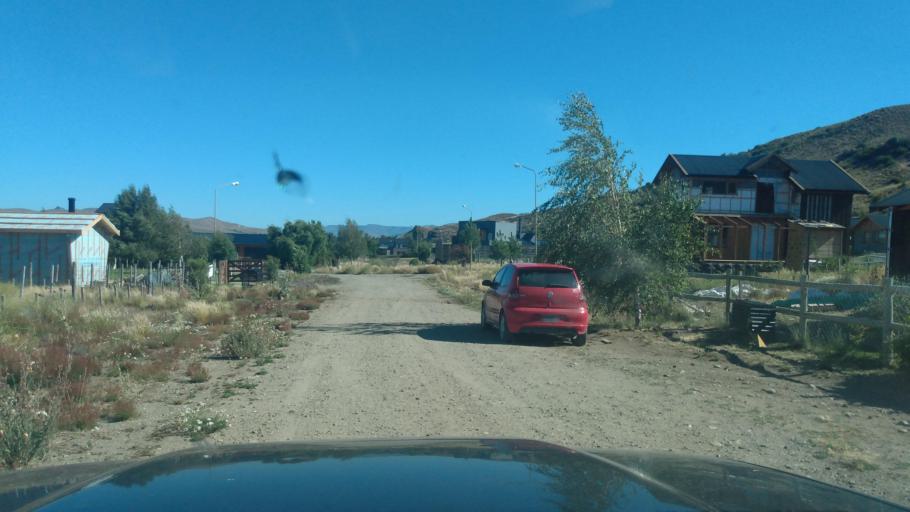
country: AR
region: Neuquen
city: Junin de los Andes
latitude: -39.9642
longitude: -71.0838
